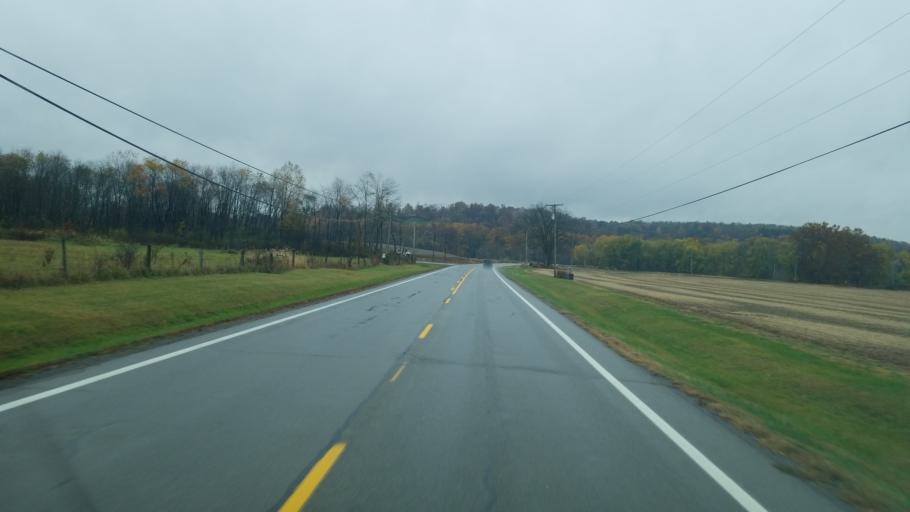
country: US
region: Ohio
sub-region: Coshocton County
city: Coshocton
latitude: 40.3278
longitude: -81.8595
